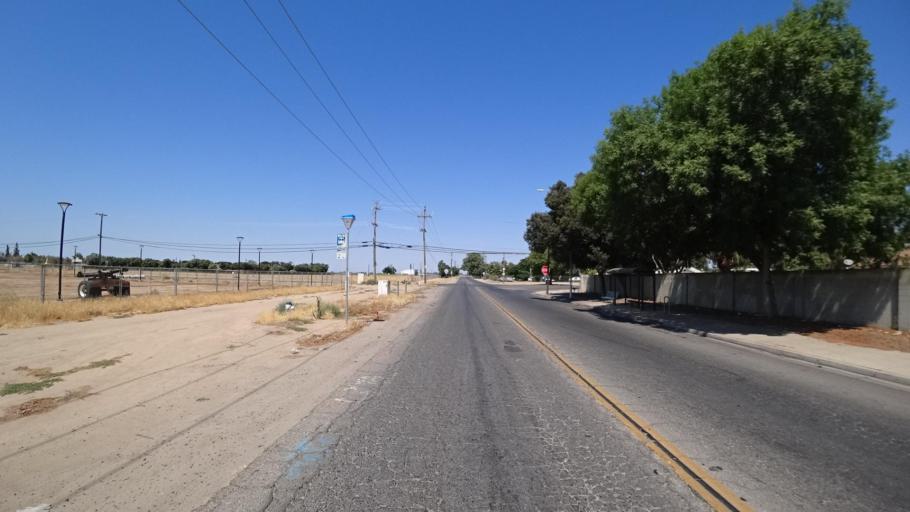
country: US
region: California
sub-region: Fresno County
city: West Park
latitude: 36.7141
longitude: -119.8082
